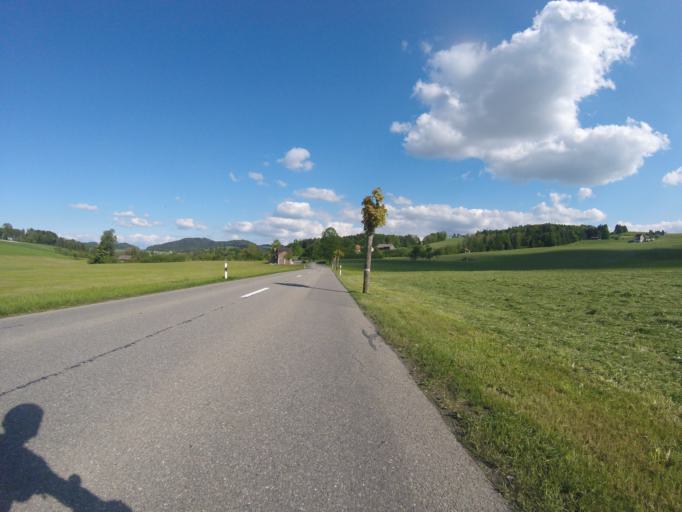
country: CH
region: Saint Gallen
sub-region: Wahlkreis Wil
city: Degersheim
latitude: 47.3873
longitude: 9.1952
